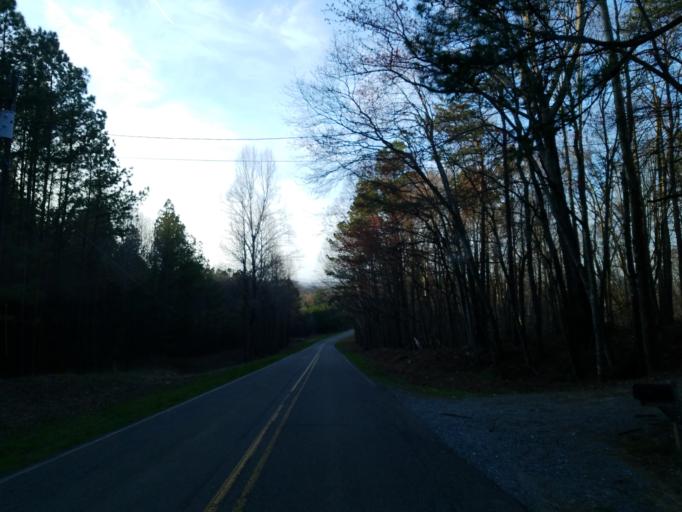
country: US
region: Georgia
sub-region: Pickens County
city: Jasper
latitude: 34.5007
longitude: -84.5211
